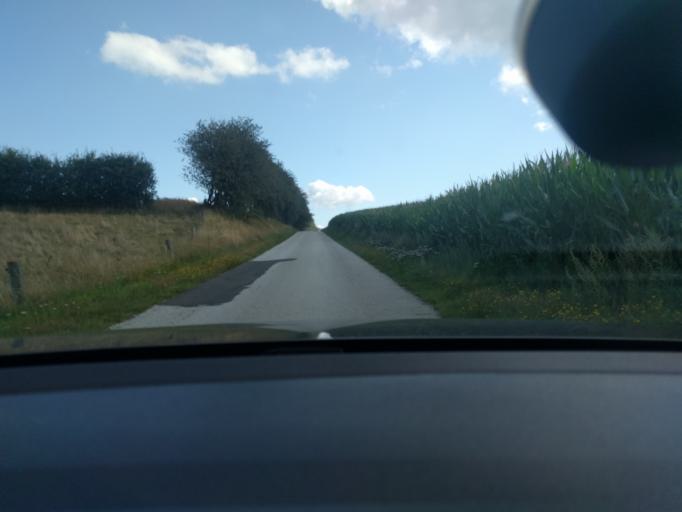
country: DK
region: Central Jutland
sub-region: Viborg Kommune
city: Viborg
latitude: 56.5026
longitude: 9.2987
